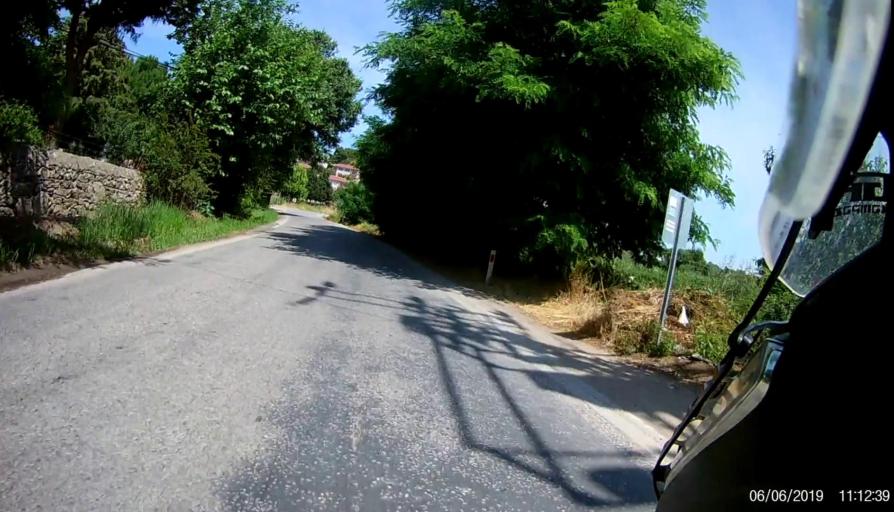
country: TR
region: Canakkale
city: Gulpinar
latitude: 39.6116
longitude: 26.1845
